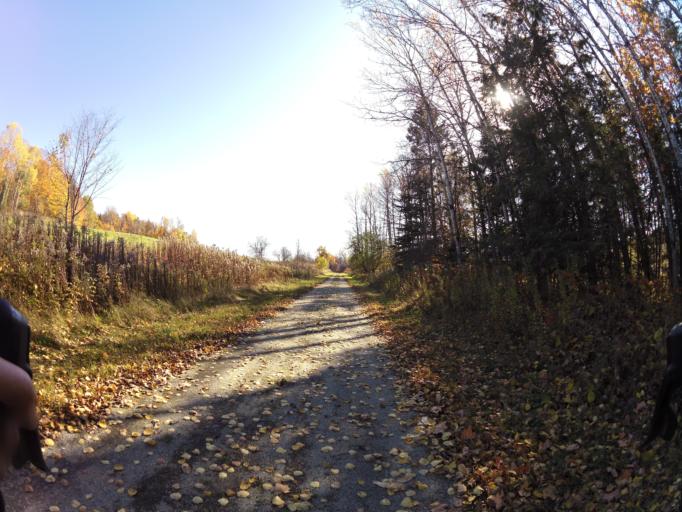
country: CA
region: Quebec
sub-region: Outaouais
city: Wakefield
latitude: 45.8383
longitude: -75.9782
